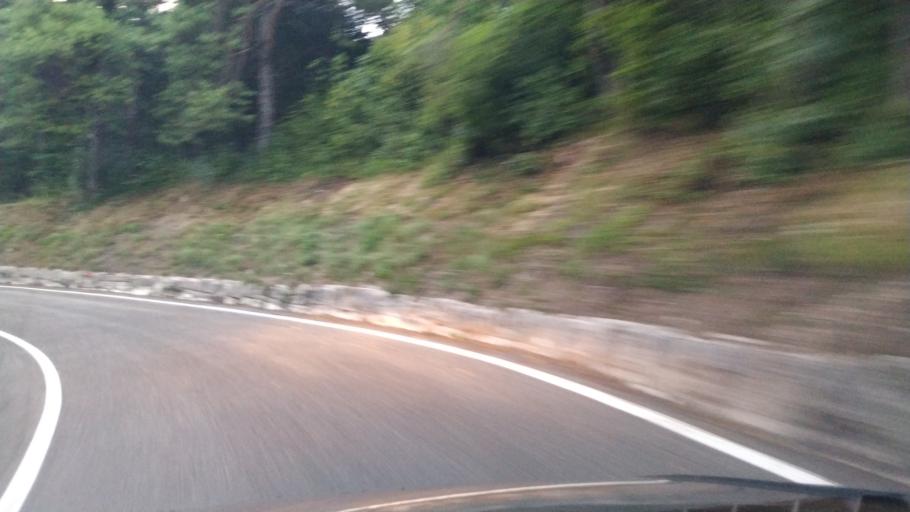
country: IT
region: Trentino-Alto Adige
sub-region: Provincia di Trento
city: Fondo
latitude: 46.4428
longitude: 11.1238
